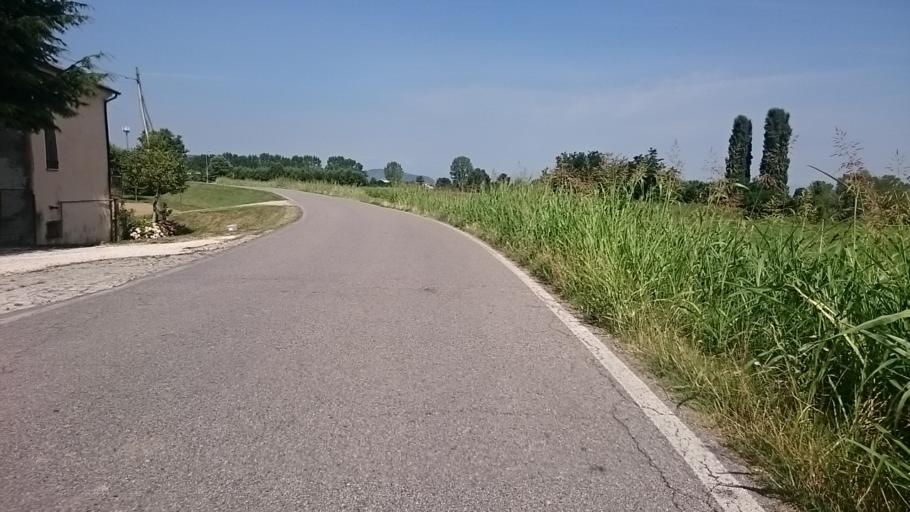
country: IT
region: Veneto
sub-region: Provincia di Padova
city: Cervarese Santa Croce
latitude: 45.4162
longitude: 11.7088
